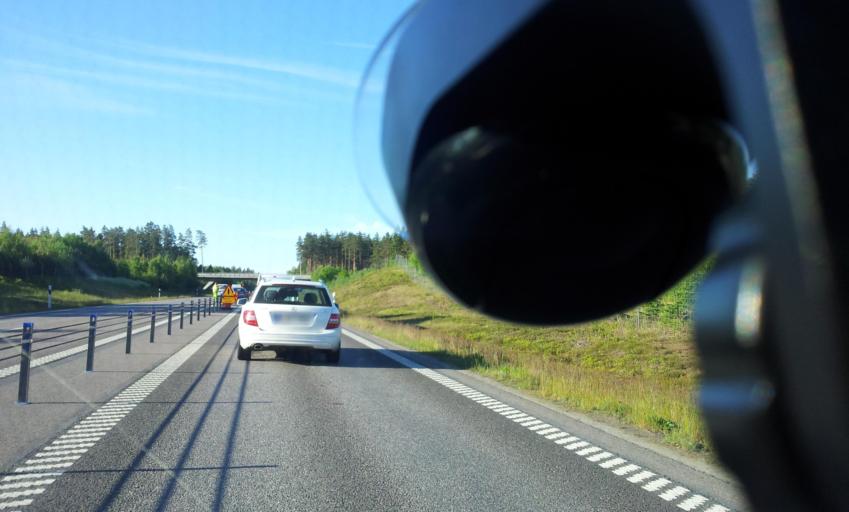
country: SE
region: Kalmar
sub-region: Torsas Kommun
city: Torsas
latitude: 56.5143
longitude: 16.0859
